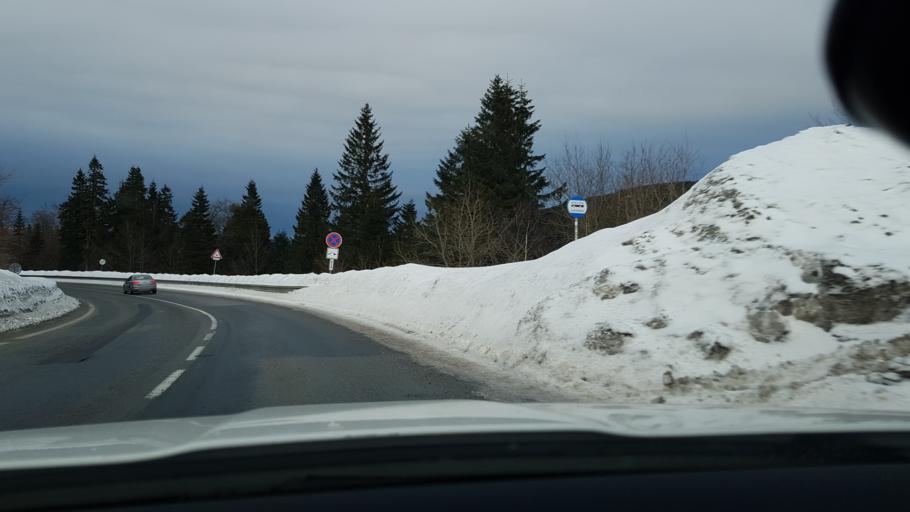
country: CZ
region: Olomoucky
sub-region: Okres Sumperk
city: Loucna nad Desnou
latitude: 50.1250
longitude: 17.1547
